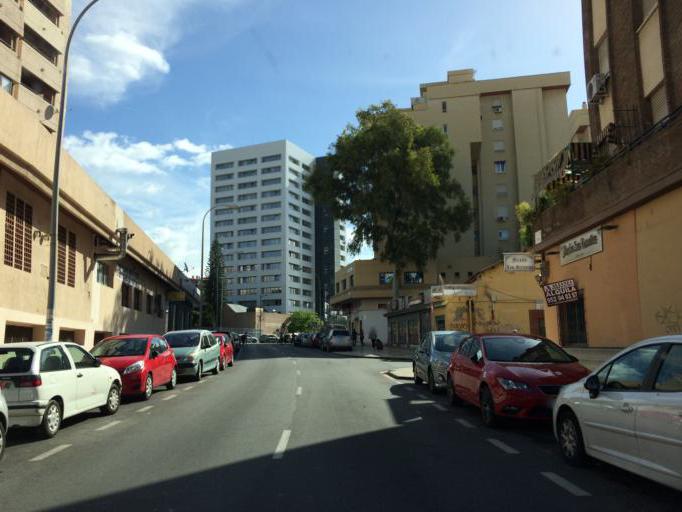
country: ES
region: Andalusia
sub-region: Provincia de Malaga
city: Malaga
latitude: 36.7146
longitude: -4.4368
